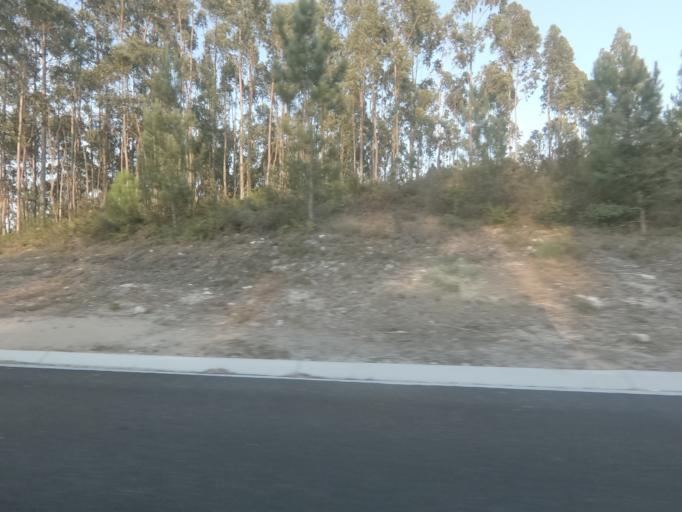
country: PT
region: Leiria
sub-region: Leiria
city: Caranguejeira
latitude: 39.7847
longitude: -8.7369
